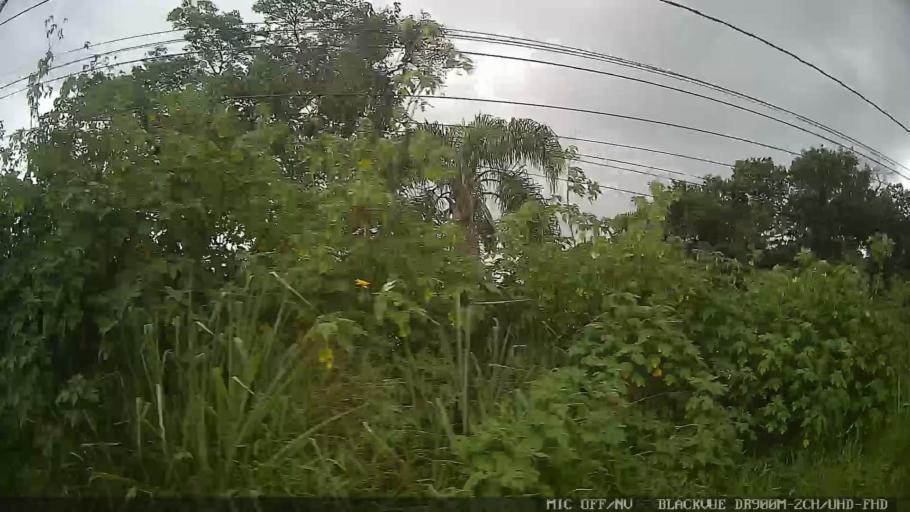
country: BR
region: Sao Paulo
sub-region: Mogi das Cruzes
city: Mogi das Cruzes
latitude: -23.5052
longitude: -46.1985
